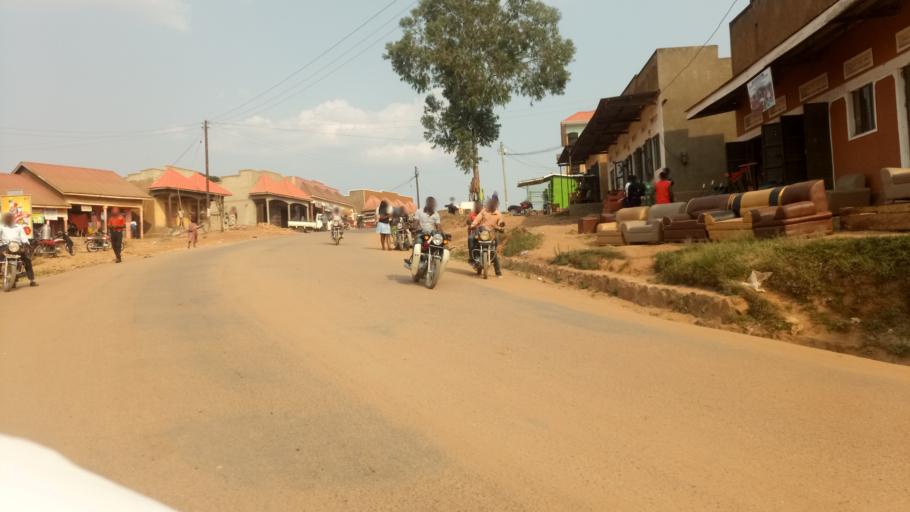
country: UG
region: Western Region
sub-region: Mbarara District
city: Mbarara
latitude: -0.6179
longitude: 30.6689
